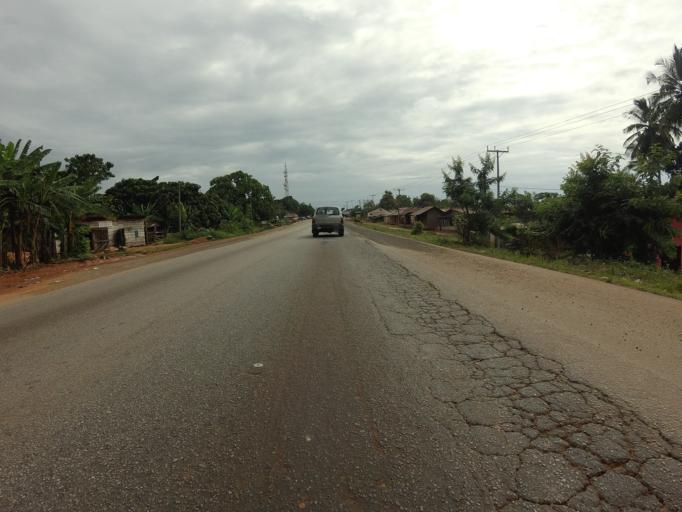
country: GH
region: Eastern
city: Nkawkaw
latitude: 6.5993
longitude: -0.8927
